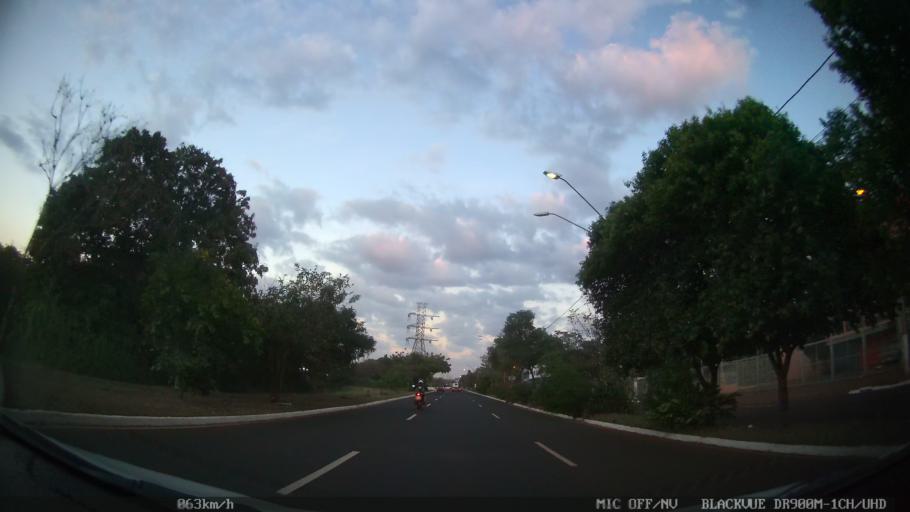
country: BR
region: Sao Paulo
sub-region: Ribeirao Preto
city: Ribeirao Preto
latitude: -21.2097
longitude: -47.7862
